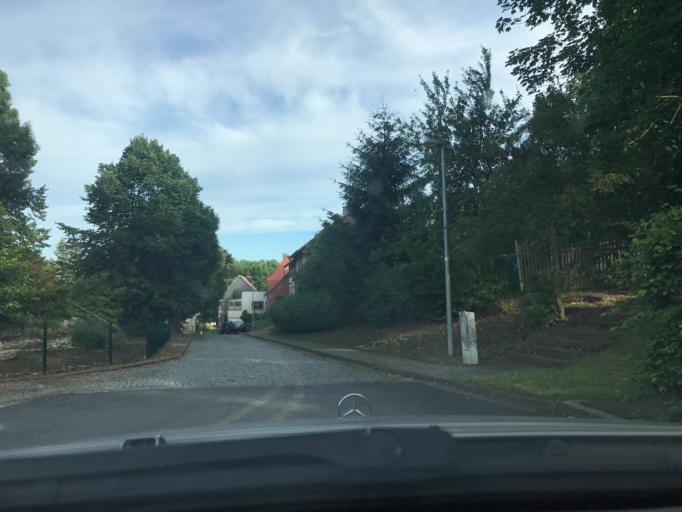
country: DE
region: Thuringia
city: Anrode
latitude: 51.2384
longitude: 10.3639
